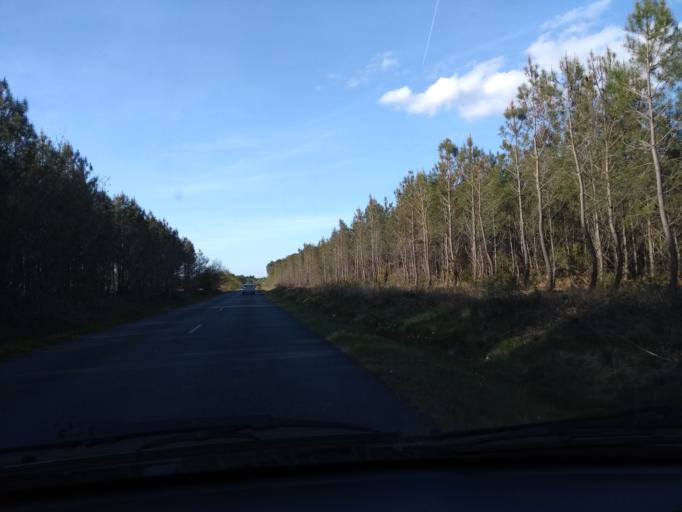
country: FR
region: Aquitaine
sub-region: Departement des Landes
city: Sanguinet
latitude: 44.4594
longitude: -1.0701
